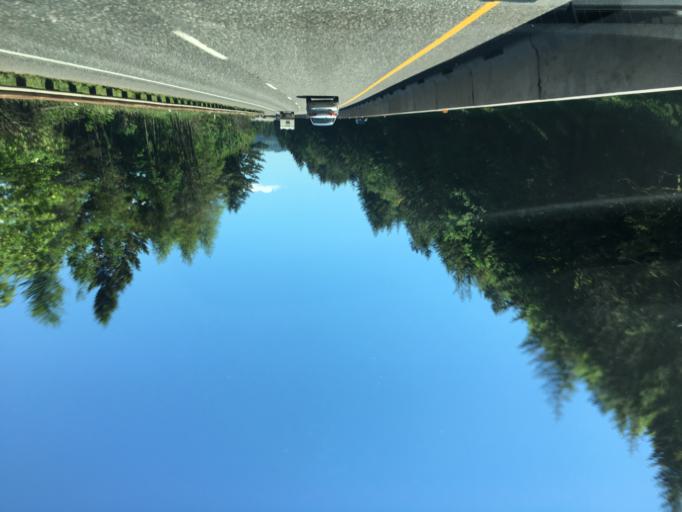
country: US
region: Washington
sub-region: Skamania County
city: Carson
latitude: 45.6938
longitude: -121.7928
